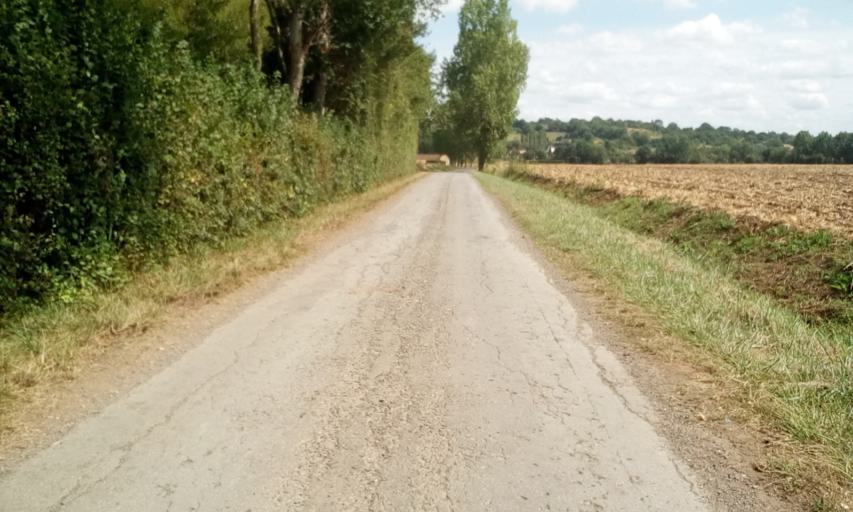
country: FR
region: Lower Normandy
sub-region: Departement du Calvados
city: Argences
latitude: 49.1343
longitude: -0.1756
